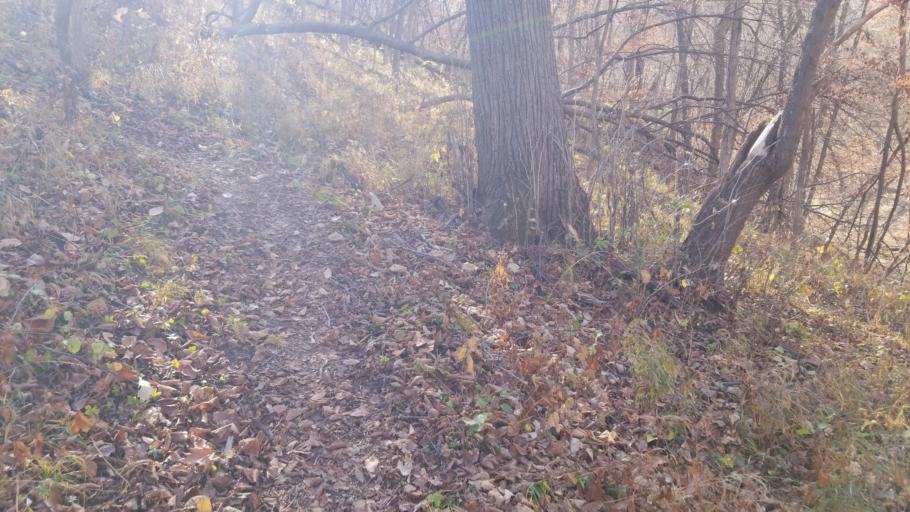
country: US
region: Nebraska
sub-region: Sarpy County
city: Bellevue
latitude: 41.1697
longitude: -95.8914
